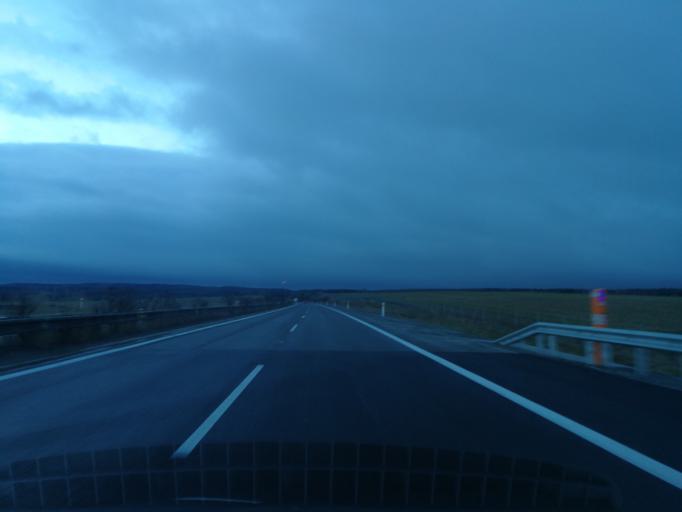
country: CZ
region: Plzensky
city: Hermanova Hut'
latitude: 49.7231
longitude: 13.0992
